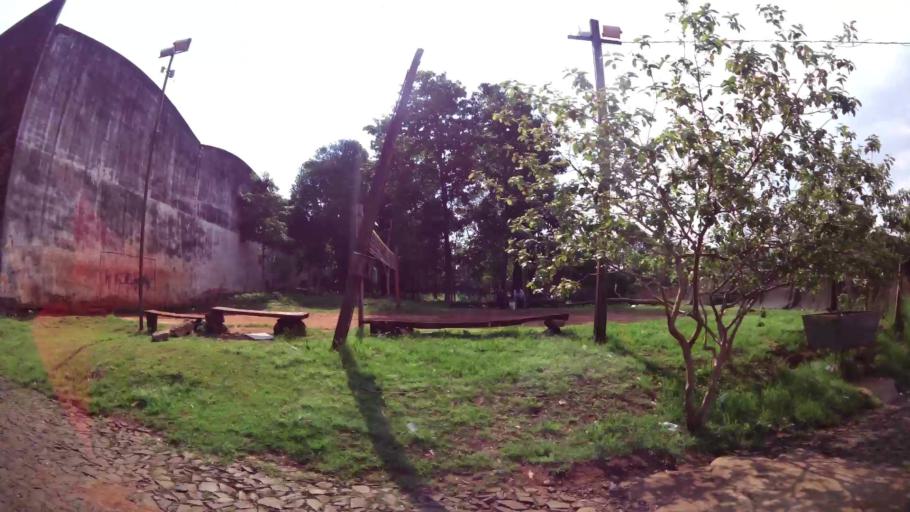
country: PY
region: Alto Parana
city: Ciudad del Este
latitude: -25.5030
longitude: -54.6307
